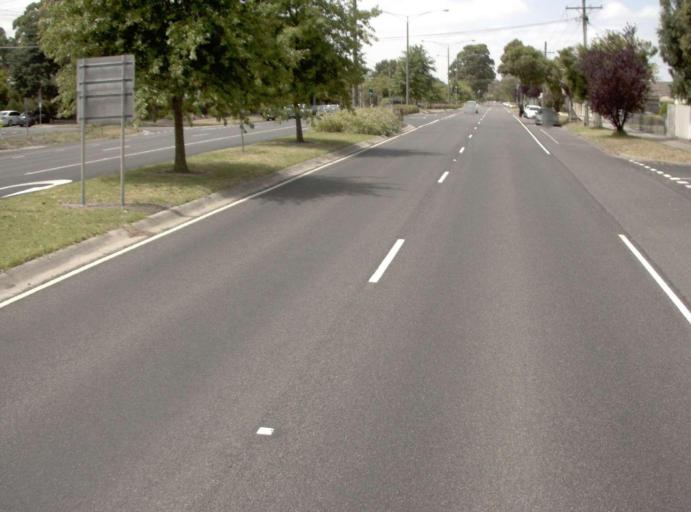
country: AU
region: Victoria
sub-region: Casey
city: Berwick
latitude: -38.0483
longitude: 145.3706
